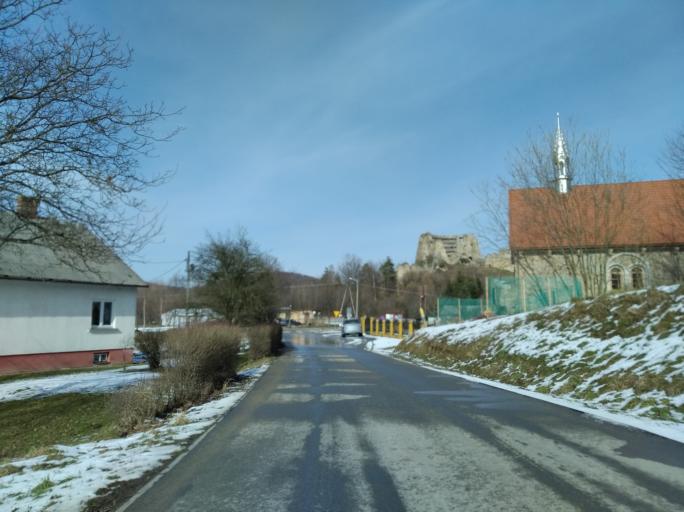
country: PL
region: Subcarpathian Voivodeship
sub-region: Powiat krosnienski
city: Korczyna
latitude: 49.7401
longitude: 21.7851
